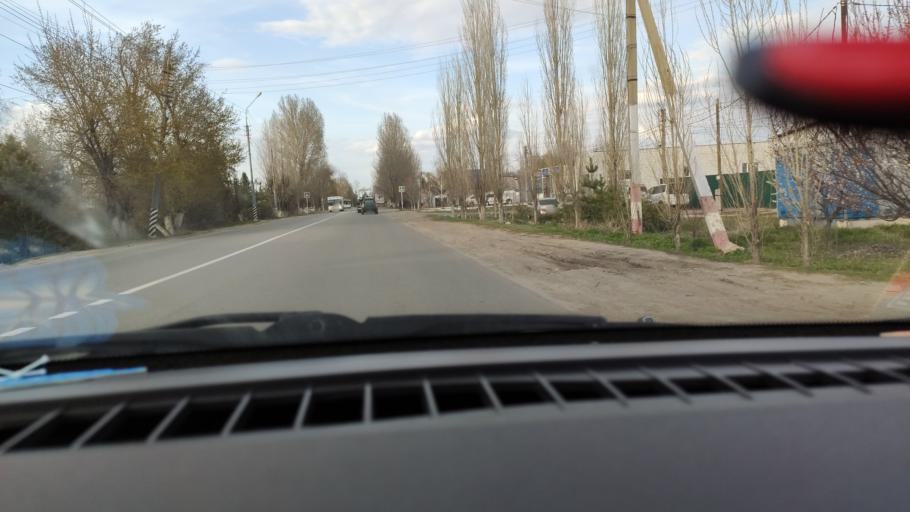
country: RU
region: Saratov
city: Privolzhskiy
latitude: 51.4346
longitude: 46.0593
